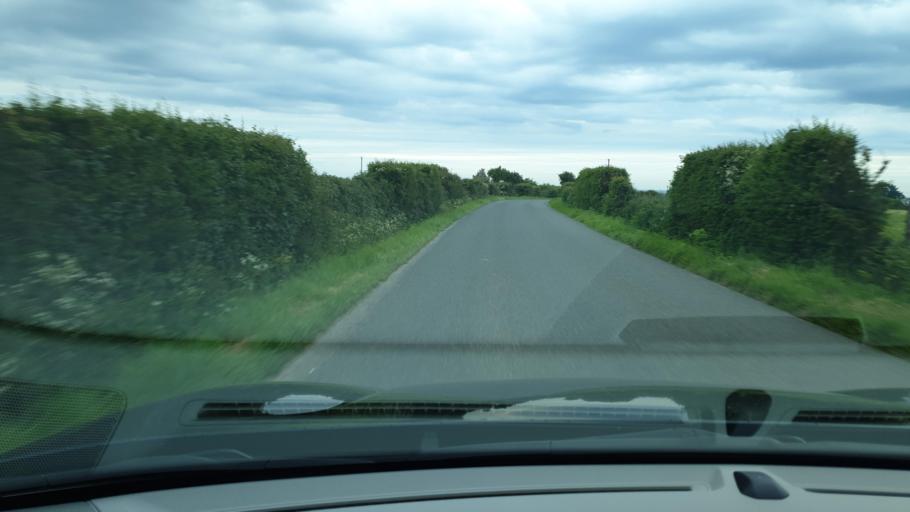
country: IE
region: Leinster
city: Lusk
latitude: 53.5564
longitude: -6.1622
